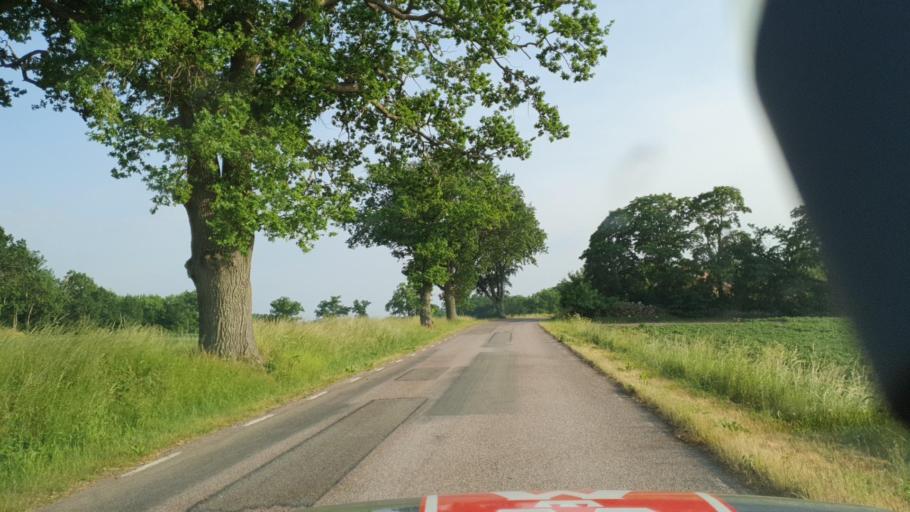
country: SE
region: Kalmar
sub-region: Kalmar Kommun
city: Ljungbyholm
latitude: 56.5184
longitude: 16.1405
